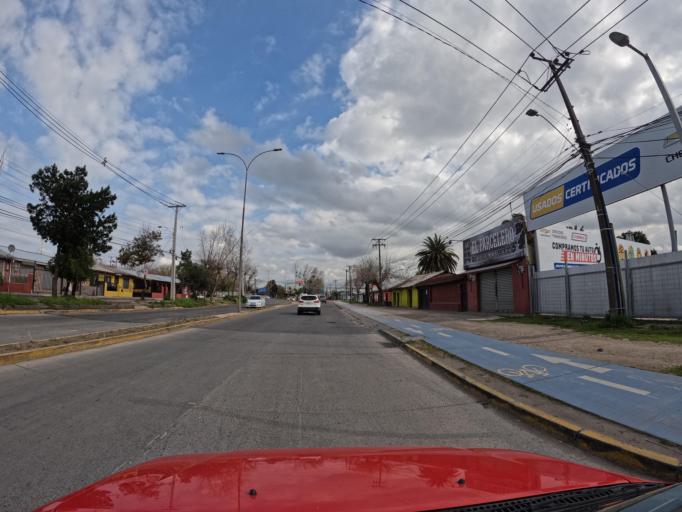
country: CL
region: Maule
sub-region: Provincia de Talca
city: Talca
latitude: -35.4284
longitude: -71.6402
